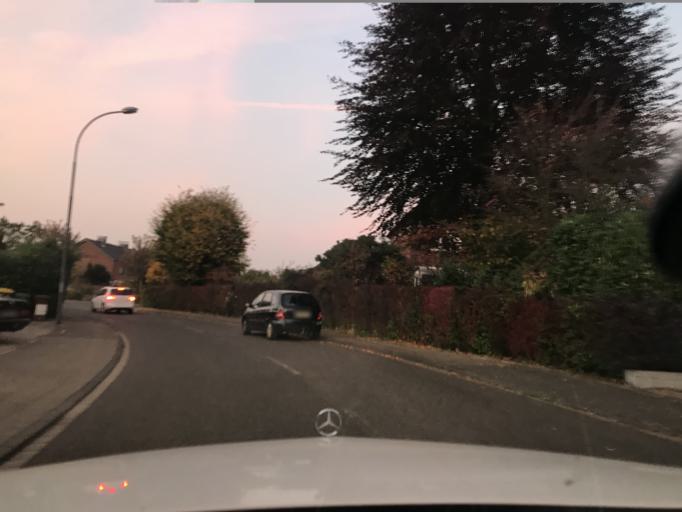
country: DE
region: North Rhine-Westphalia
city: Tonisvorst
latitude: 51.3259
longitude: 6.5083
